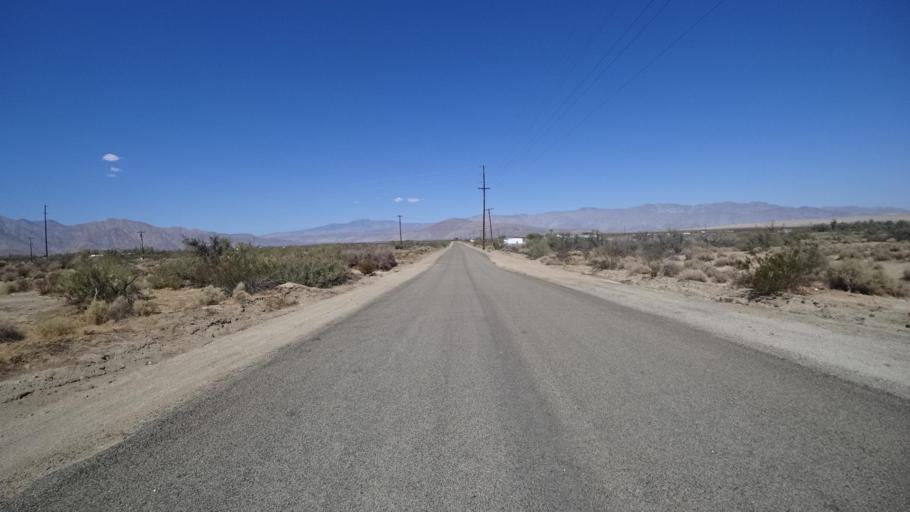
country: US
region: California
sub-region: San Diego County
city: Borrego Springs
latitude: 33.2199
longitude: -116.3302
